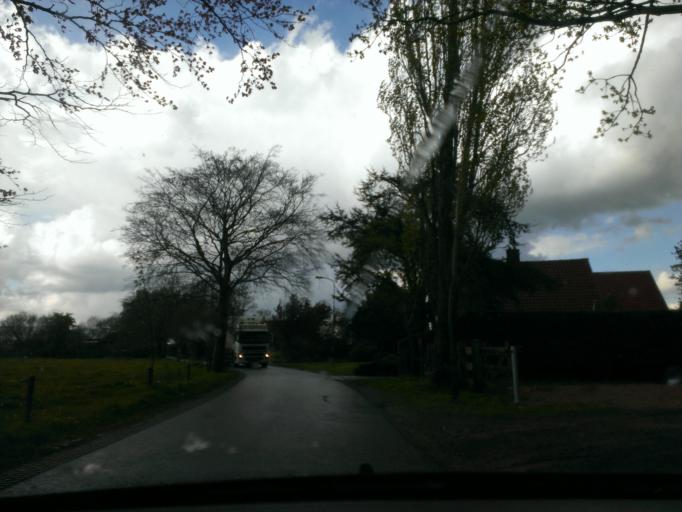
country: NL
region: Gelderland
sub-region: Gemeente Heerde
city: Heerde
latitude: 52.3693
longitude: 6.0459
